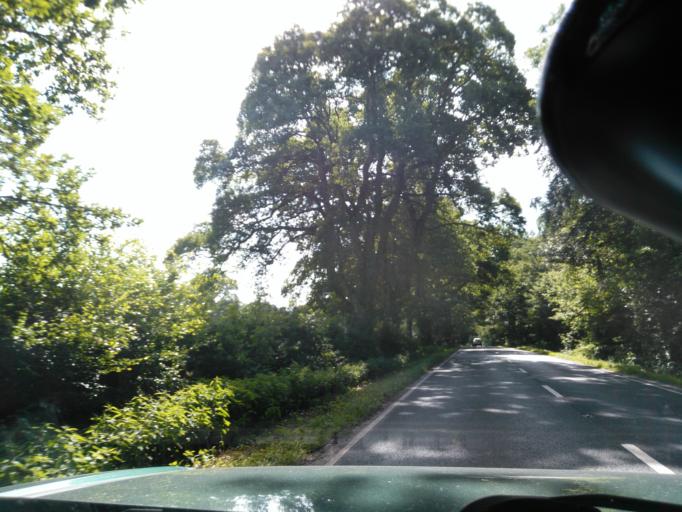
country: GB
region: England
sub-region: Hampshire
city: West Wellow
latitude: 50.9602
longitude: -1.5573
